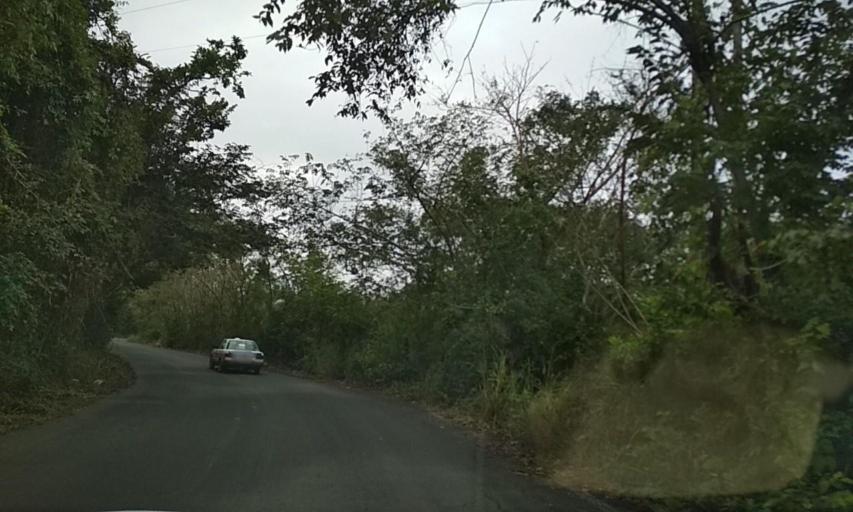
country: MX
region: Veracruz
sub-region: Coatzintla
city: Manuel Maria Contreras
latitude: 20.4455
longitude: -97.5020
